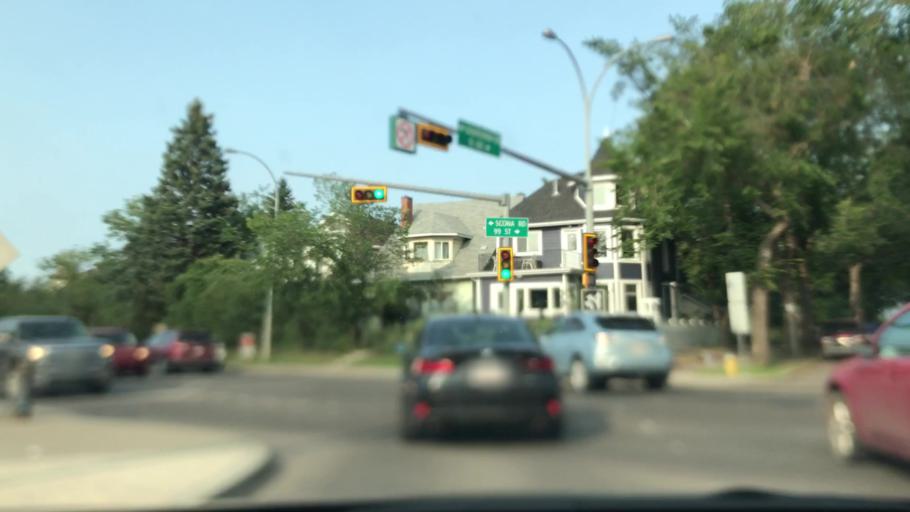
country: CA
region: Alberta
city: Edmonton
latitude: 53.5274
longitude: -113.4862
